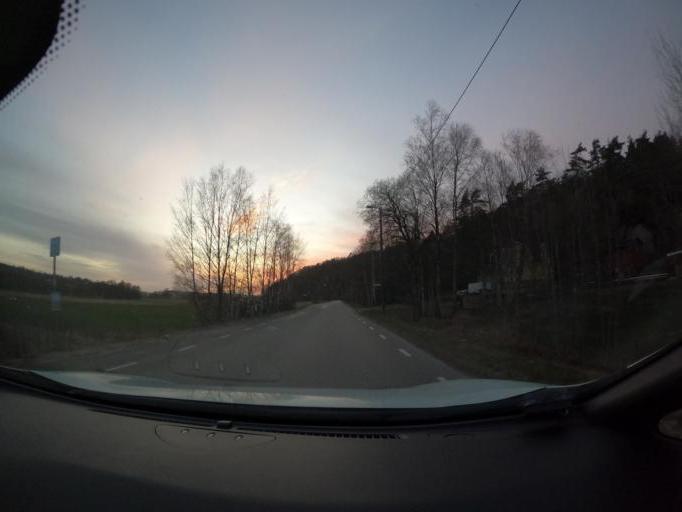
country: SE
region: Vaestra Goetaland
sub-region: Harryda Kommun
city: Molnlycke
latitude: 57.6050
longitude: 12.1749
